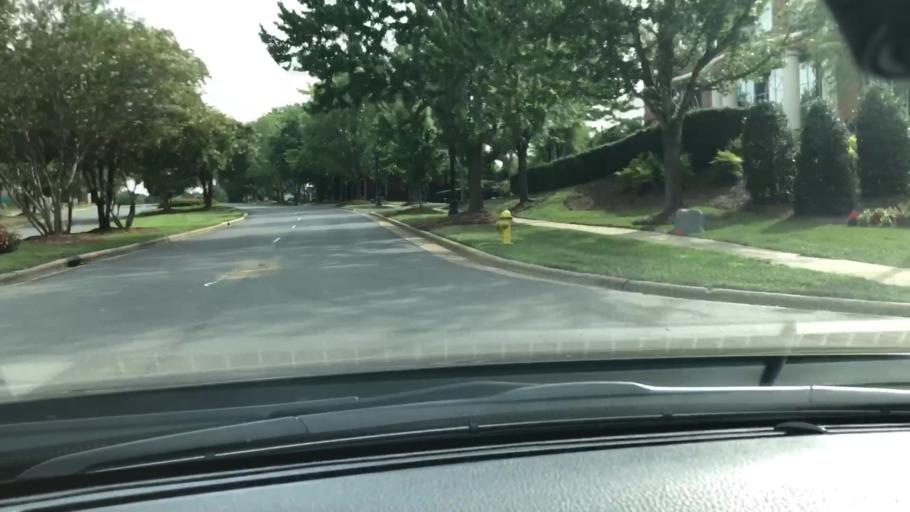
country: US
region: North Carolina
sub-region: Mecklenburg County
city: Charlotte
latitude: 35.1488
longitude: -80.8246
